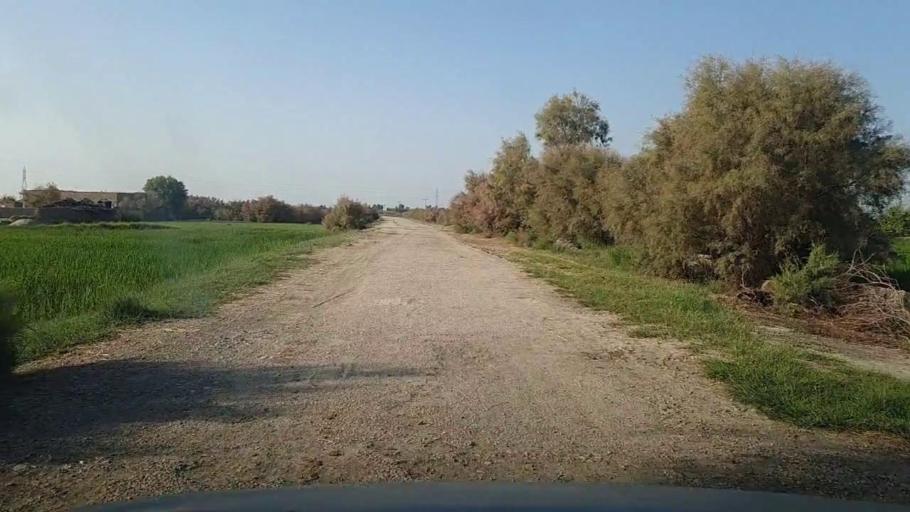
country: PK
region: Sindh
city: Kandhkot
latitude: 28.3040
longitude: 69.3288
